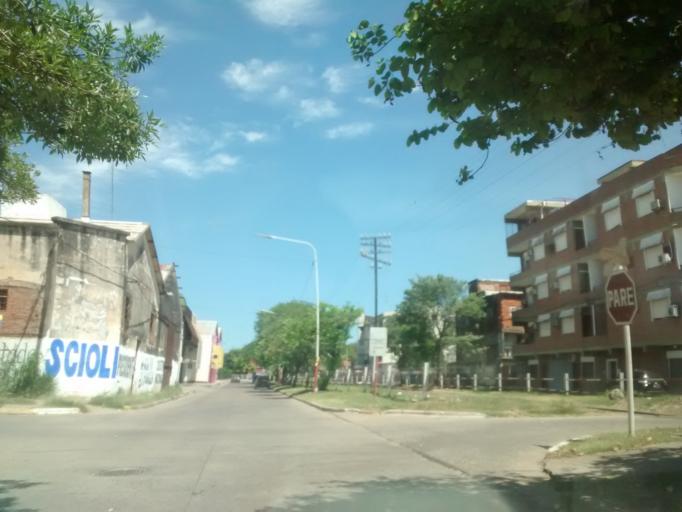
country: AR
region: Chaco
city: Resistencia
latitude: -27.4603
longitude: -58.9849
